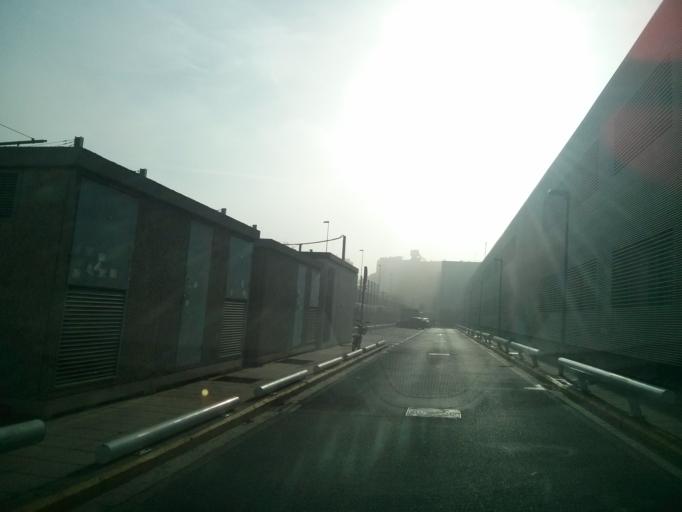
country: ES
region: Valencia
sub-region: Provincia de Valencia
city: Alboraya
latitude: 39.4798
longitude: -0.3355
